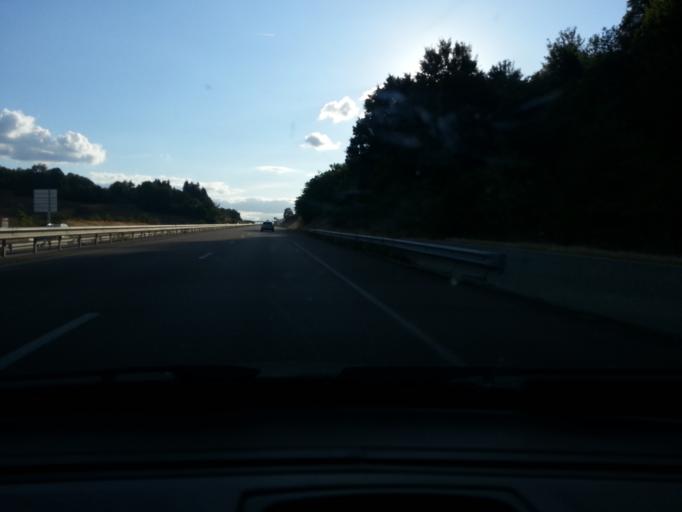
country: FR
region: Bourgogne
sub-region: Departement de Saone-et-Loire
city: Buxy
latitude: 46.7546
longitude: 4.6836
